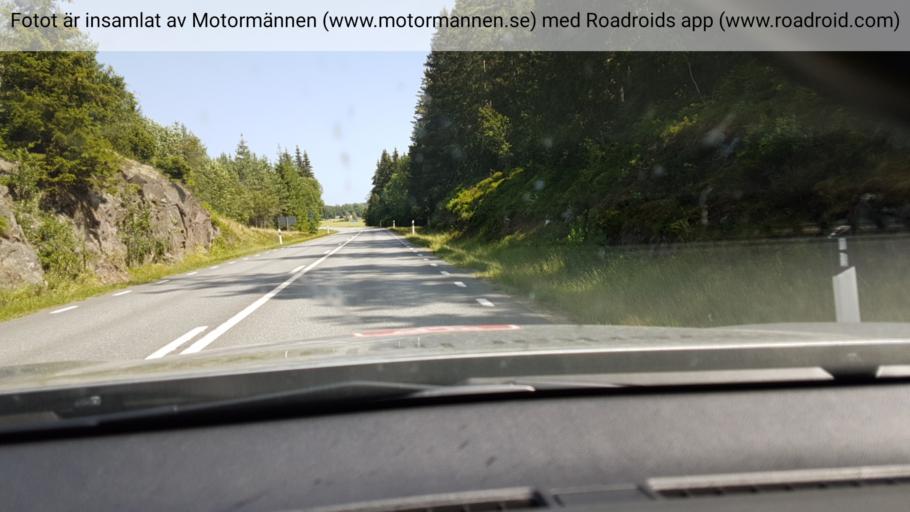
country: SE
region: Joenkoeping
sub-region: Nassjo Kommun
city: Bodafors
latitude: 57.4607
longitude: 14.7475
